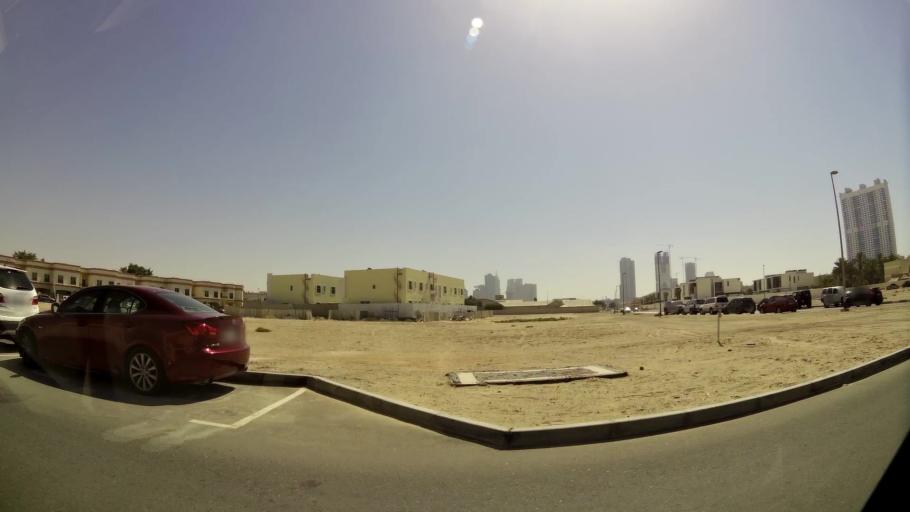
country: AE
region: Dubai
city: Dubai
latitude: 25.1084
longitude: 55.1957
